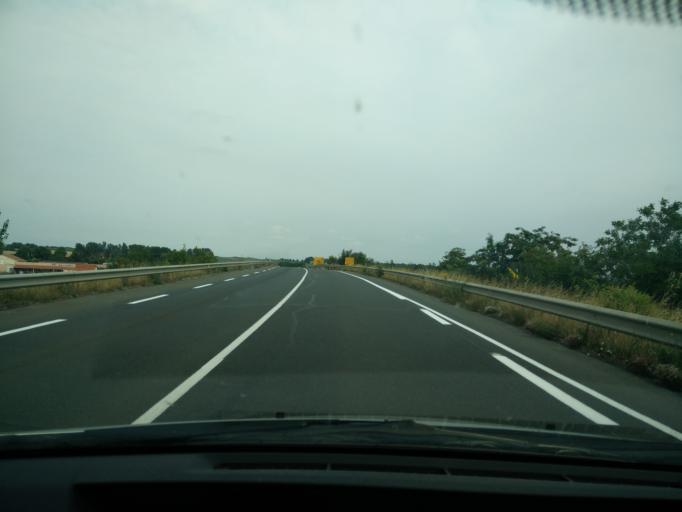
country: FR
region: Poitou-Charentes
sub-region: Departement des Deux-Sevres
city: Louzy
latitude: 47.0099
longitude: -0.1963
